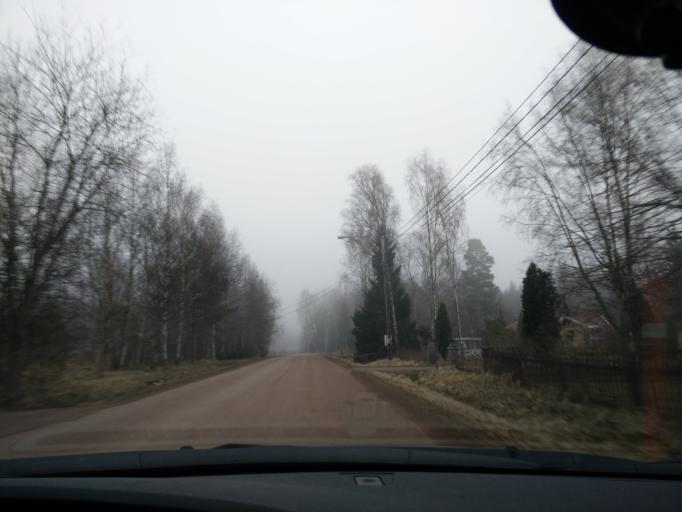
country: AX
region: Mariehamns stad
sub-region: Mariehamn
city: Mariehamn
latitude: 60.1009
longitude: 19.9051
